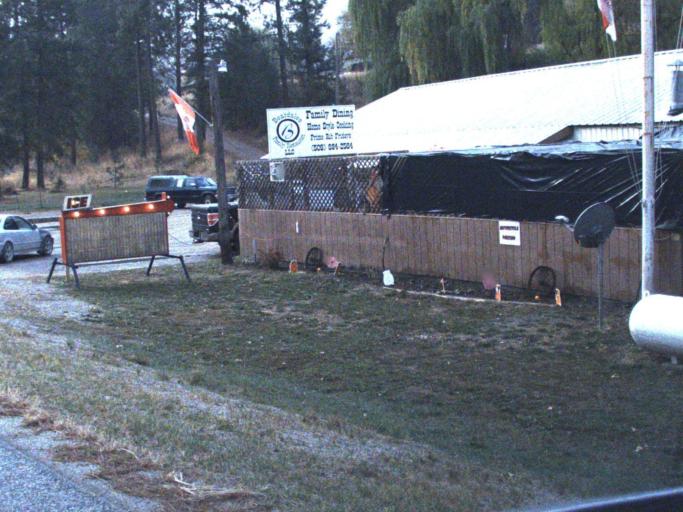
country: CA
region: British Columbia
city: Grand Forks
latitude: 48.8645
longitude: -118.2056
